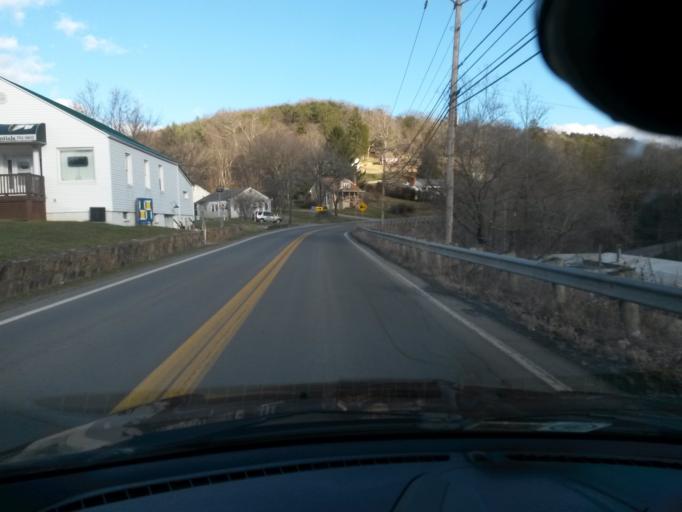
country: US
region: Virginia
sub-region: Giles County
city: Narrows
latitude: 37.3961
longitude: -80.7918
